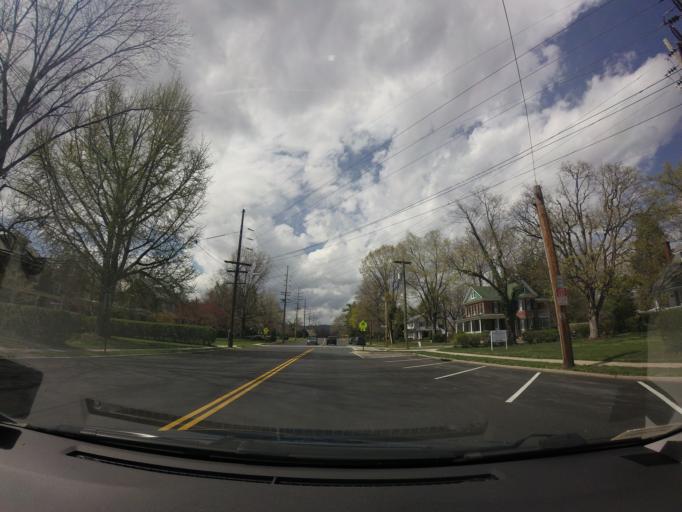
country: US
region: Maryland
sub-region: Frederick County
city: Frederick
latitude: 39.4210
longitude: -77.4215
